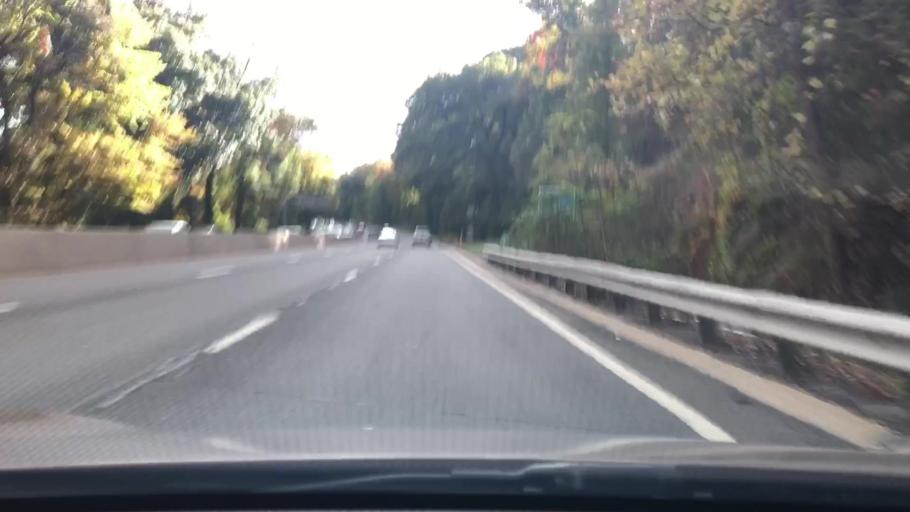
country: US
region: New York
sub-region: Westchester County
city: Yonkers
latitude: 40.9212
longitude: -73.8820
